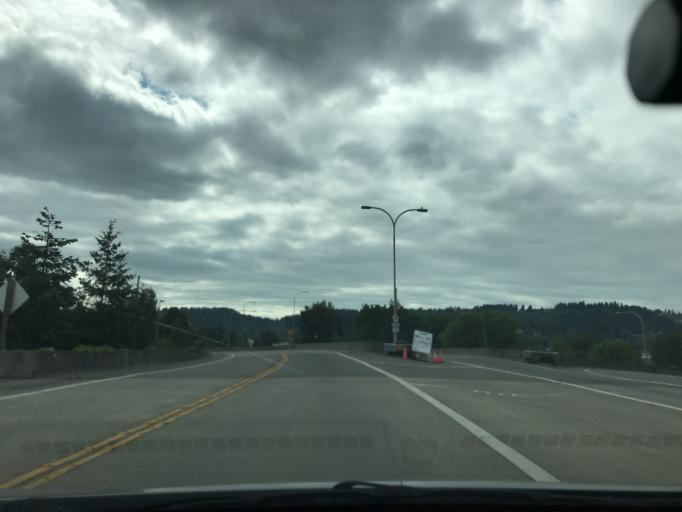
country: US
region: Washington
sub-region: King County
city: Auburn
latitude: 47.3049
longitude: -122.2320
